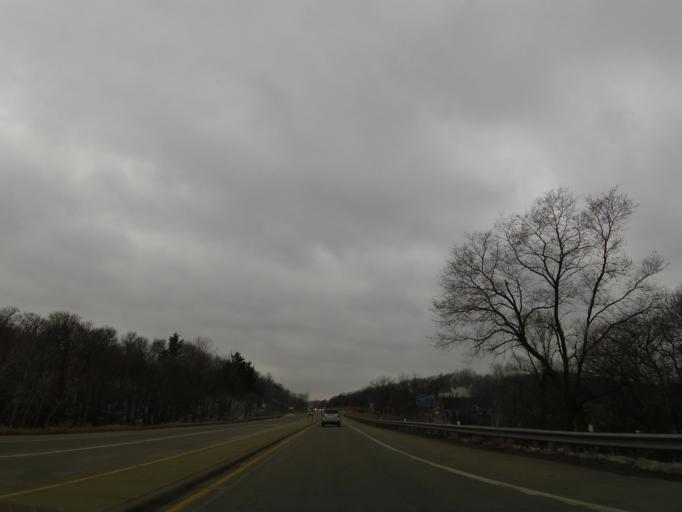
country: US
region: Minnesota
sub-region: Scott County
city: Prior Lake
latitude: 44.7258
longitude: -93.4043
